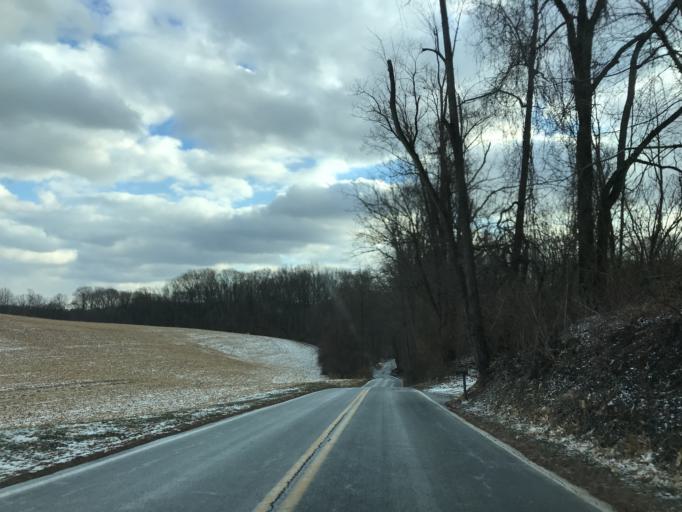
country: US
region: Maryland
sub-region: Harford County
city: Bel Air North
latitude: 39.6357
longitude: -76.3764
